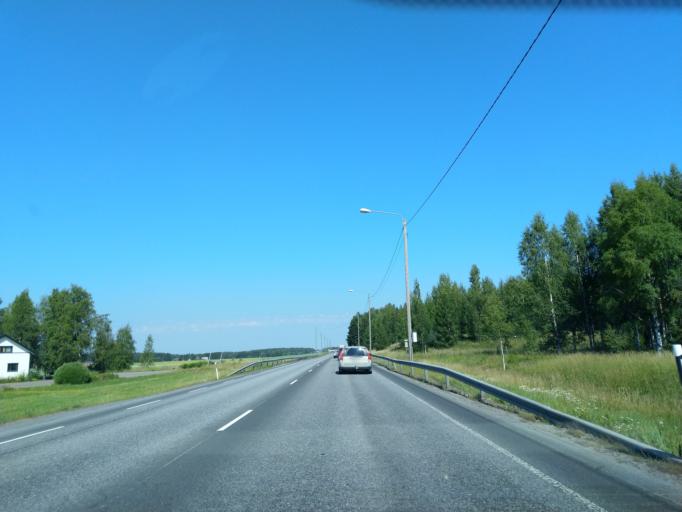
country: FI
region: Satakunta
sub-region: Pori
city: Nakkila
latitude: 61.3659
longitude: 21.9879
